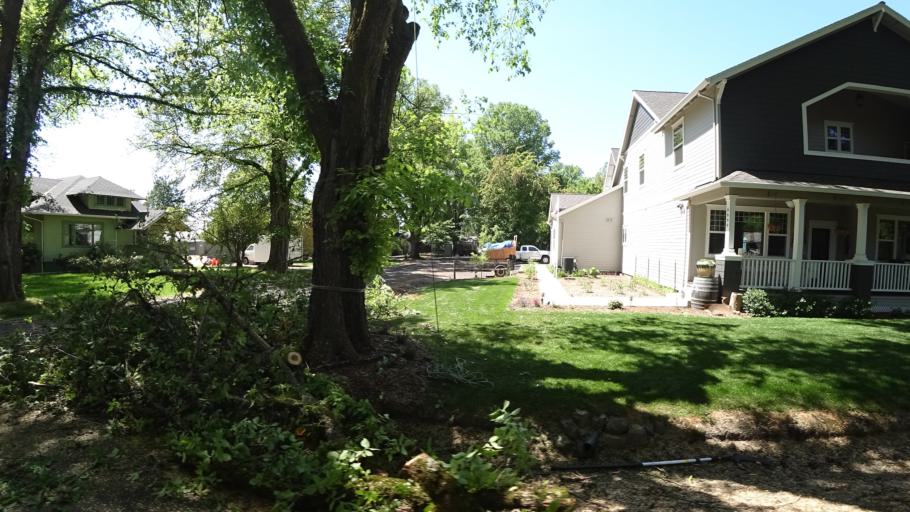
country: US
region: Oregon
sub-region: Washington County
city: Rockcreek
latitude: 45.5278
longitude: -122.9119
